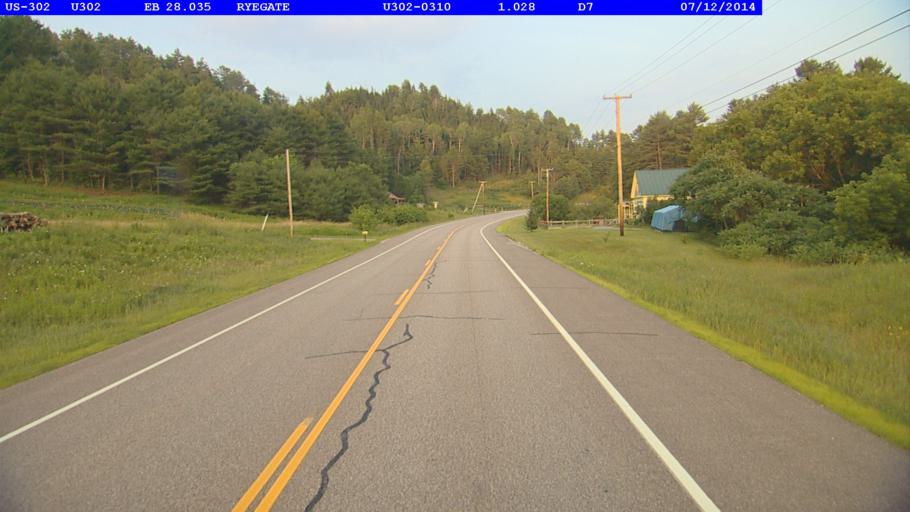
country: US
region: New Hampshire
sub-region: Grafton County
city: Woodsville
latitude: 44.1971
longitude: -72.1542
